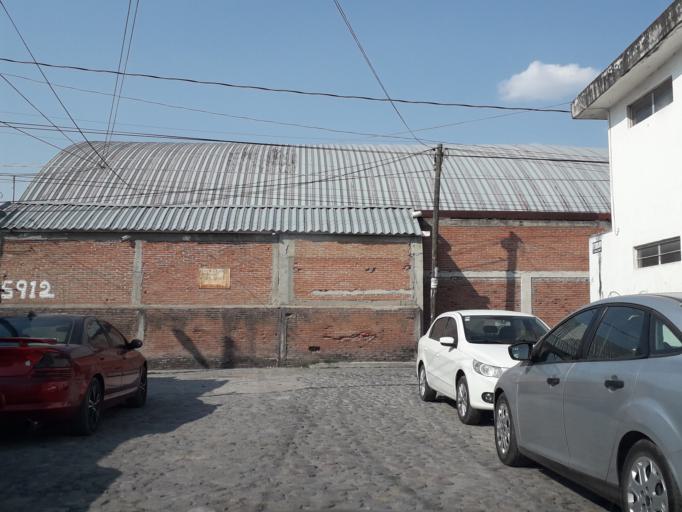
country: MX
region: Puebla
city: Puebla
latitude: 19.0151
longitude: -98.2125
